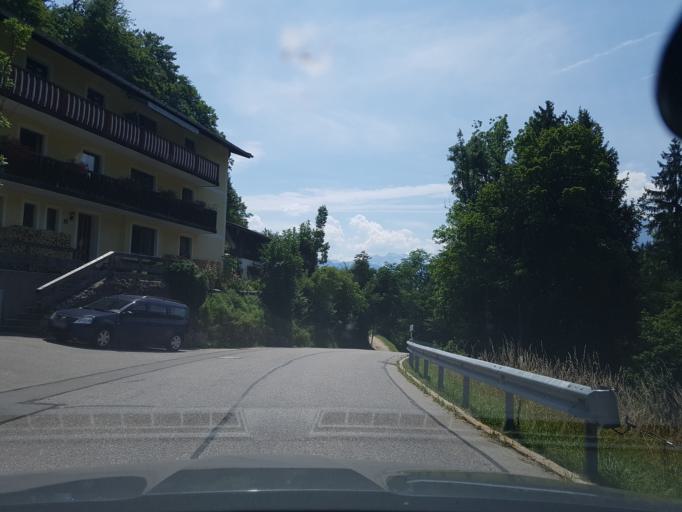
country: DE
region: Bavaria
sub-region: Upper Bavaria
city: Berchtesgaden
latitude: 47.6528
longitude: 13.0023
